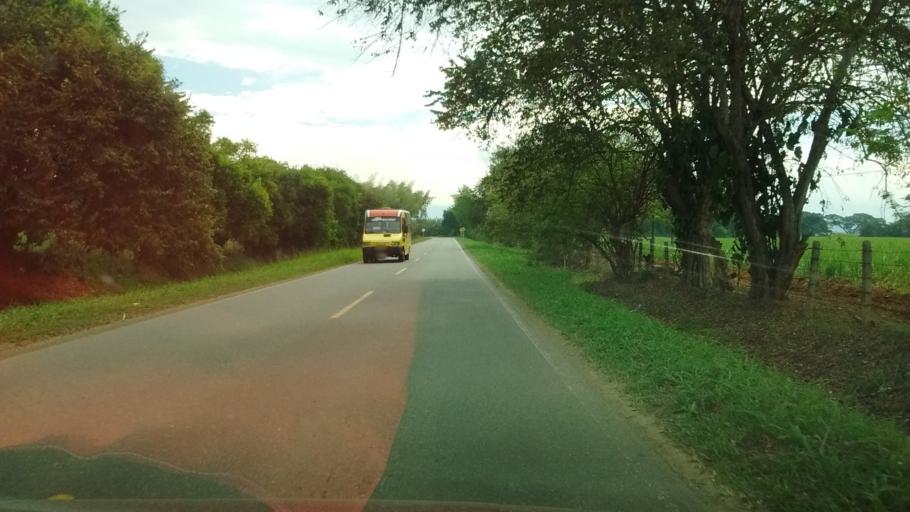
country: CO
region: Cauca
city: Caloto
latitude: 3.0466
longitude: -76.4485
